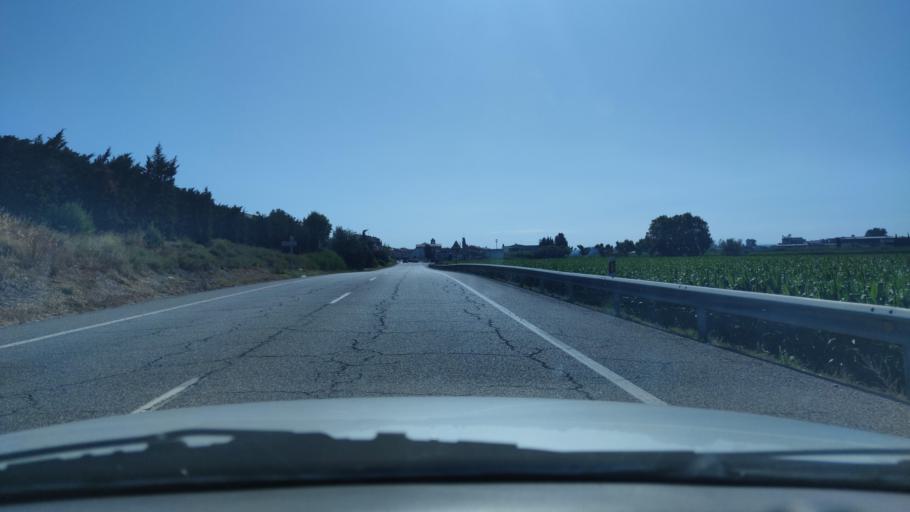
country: ES
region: Catalonia
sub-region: Provincia de Lleida
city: Sidamon
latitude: 41.6288
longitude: 0.7707
